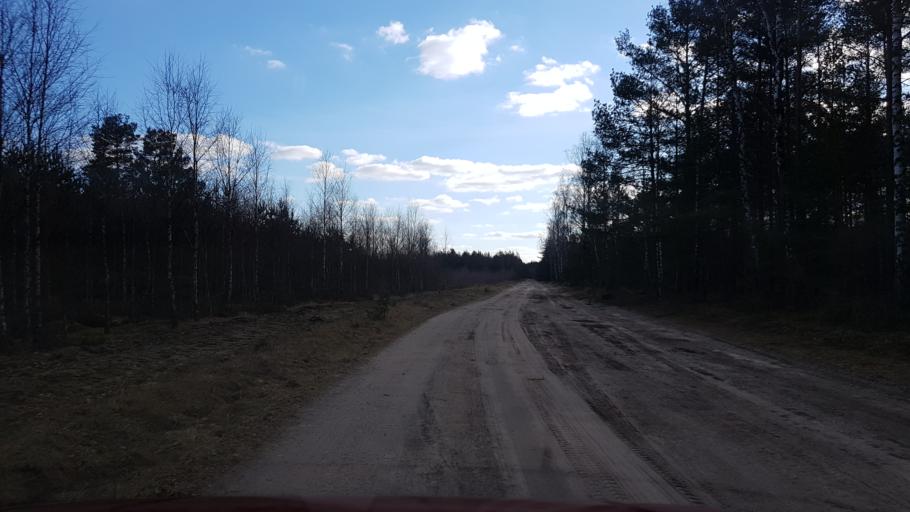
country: PL
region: Greater Poland Voivodeship
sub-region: Powiat zlotowski
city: Sypniewo
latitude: 53.5277
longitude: 16.6478
